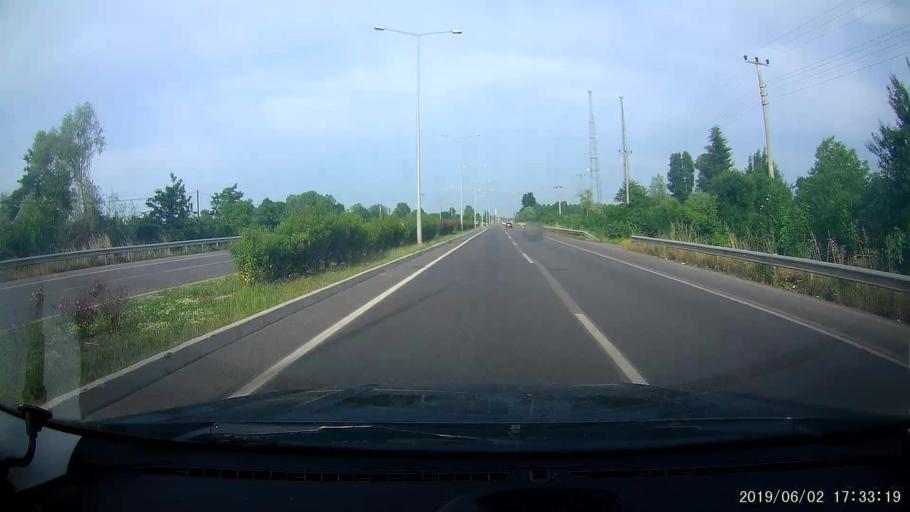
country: TR
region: Samsun
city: Carsamba
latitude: 41.2208
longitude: 36.8461
